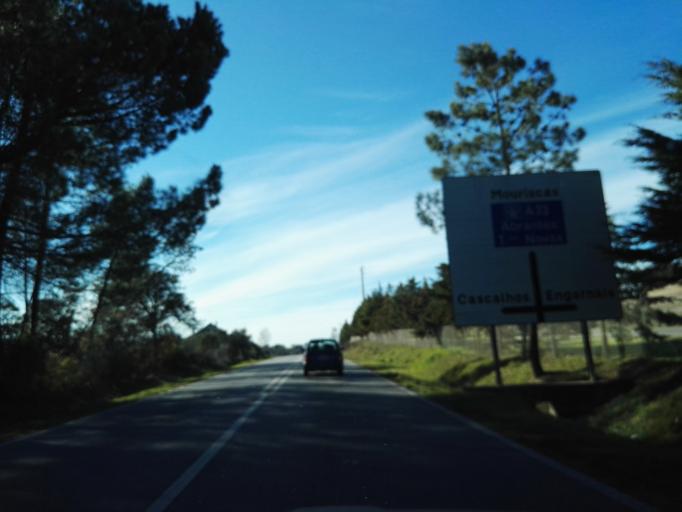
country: PT
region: Santarem
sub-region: Abrantes
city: Alferrarede
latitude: 39.4758
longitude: -8.0780
